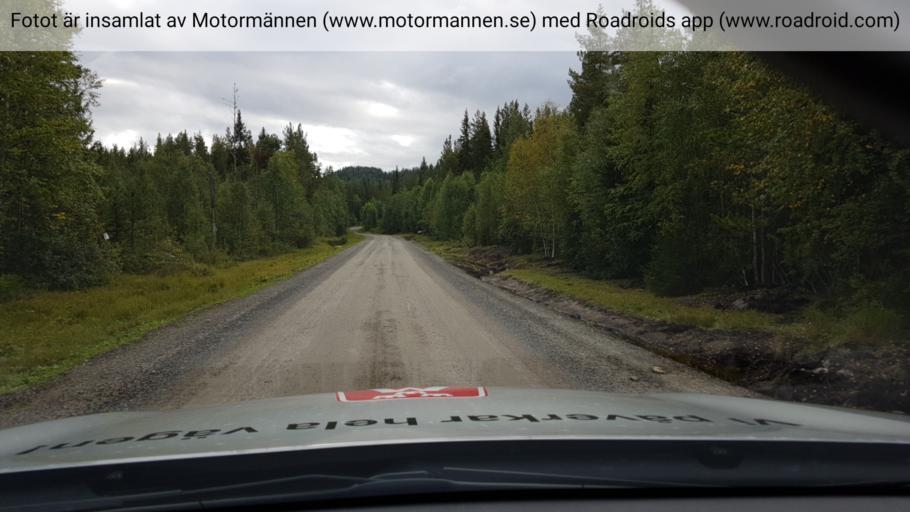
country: SE
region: Jaemtland
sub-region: Ragunda Kommun
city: Hammarstrand
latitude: 62.9259
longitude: 16.1236
